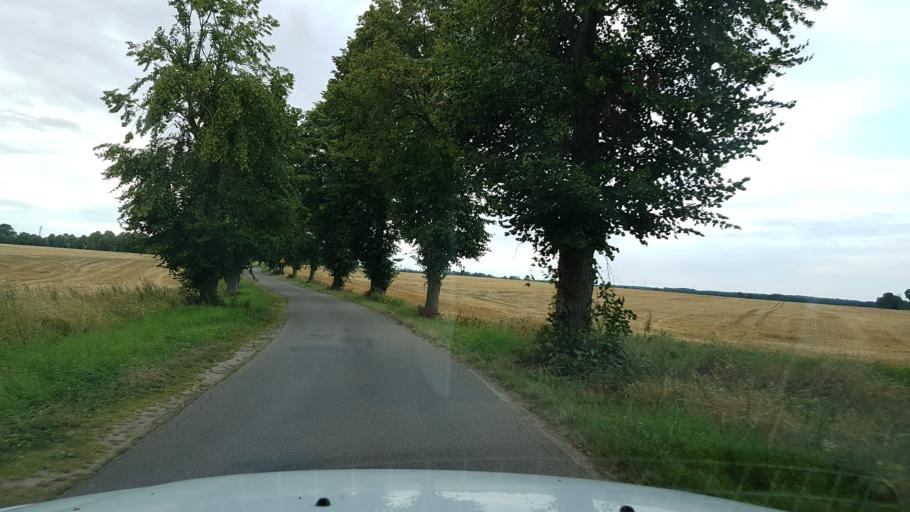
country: PL
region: West Pomeranian Voivodeship
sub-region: Powiat bialogardzki
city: Karlino
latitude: 54.1134
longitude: 15.8788
